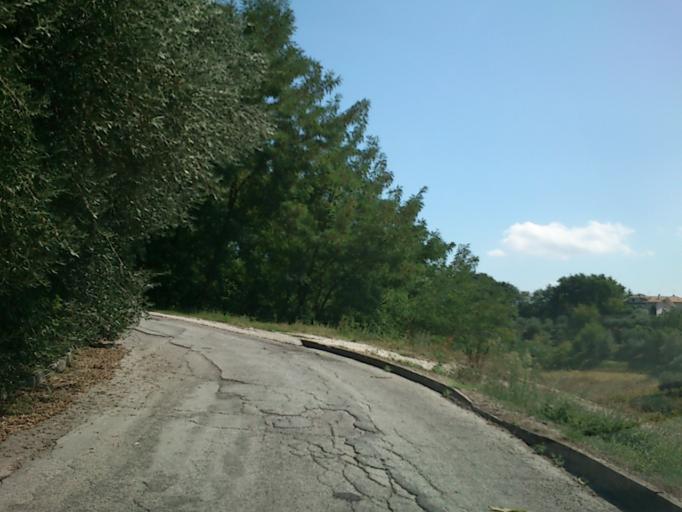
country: IT
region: The Marches
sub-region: Provincia di Pesaro e Urbino
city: Saltara
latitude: 43.7525
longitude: 12.8975
